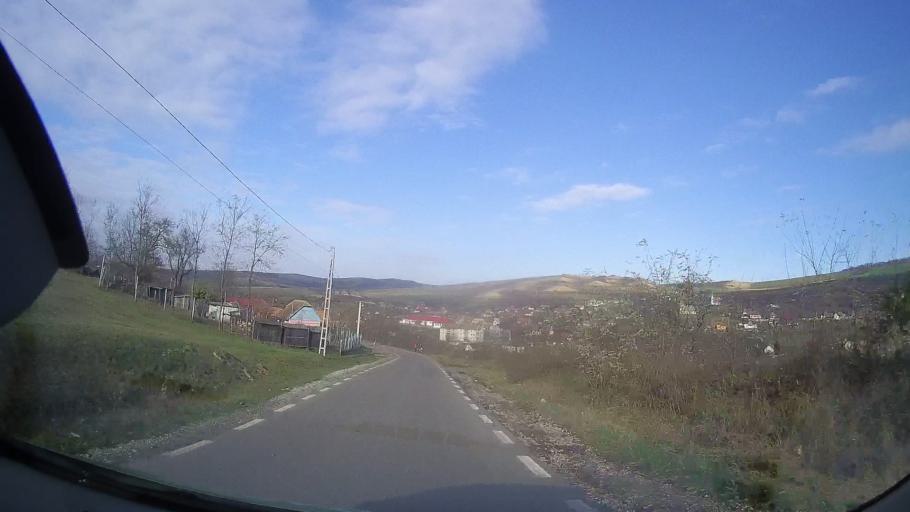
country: RO
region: Mures
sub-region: Comuna Sanger
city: Sanger
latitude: 46.5544
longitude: 24.1423
